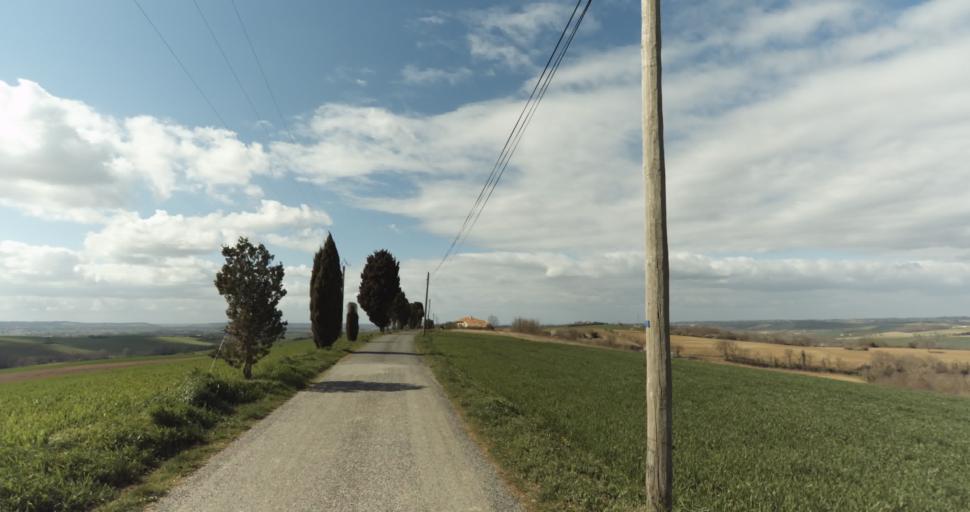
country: FR
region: Midi-Pyrenees
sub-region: Departement de la Haute-Garonne
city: Auterive
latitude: 43.3800
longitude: 1.4946
